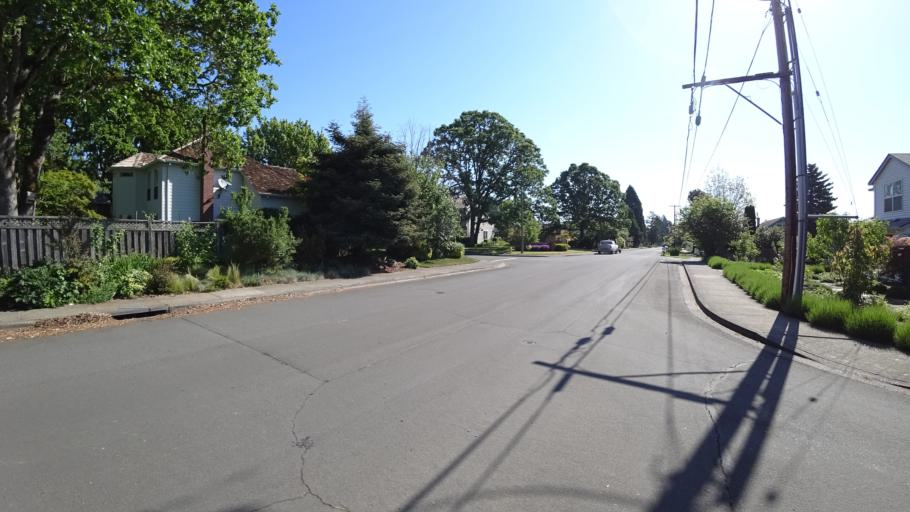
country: US
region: Oregon
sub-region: Washington County
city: Rockcreek
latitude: 45.5239
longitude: -122.9188
